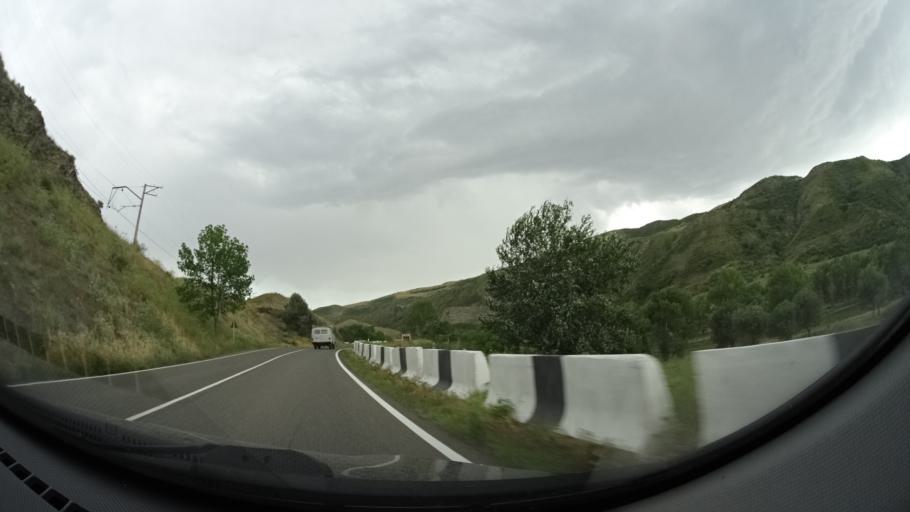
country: GE
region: Samtskhe-Javakheti
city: Akhaltsikhe
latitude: 41.6912
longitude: 43.0982
